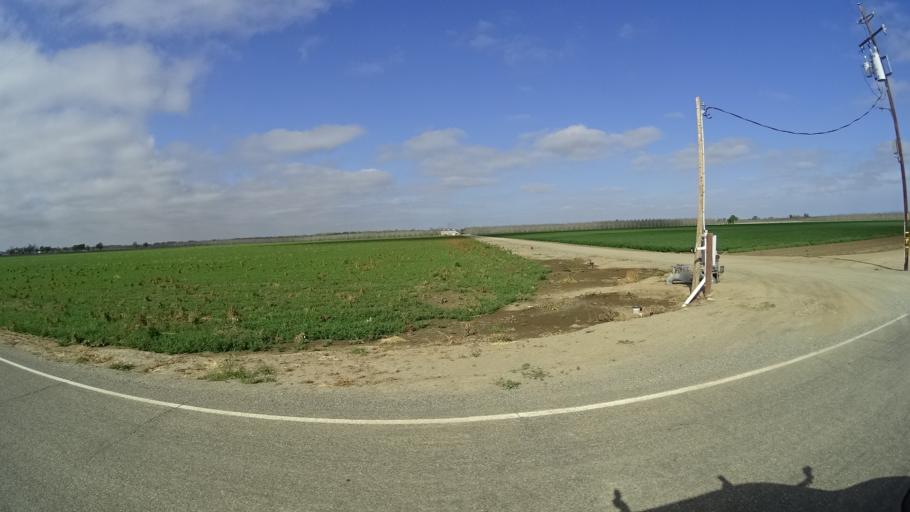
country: US
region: California
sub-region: Colusa County
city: Colusa
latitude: 39.4359
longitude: -121.9671
